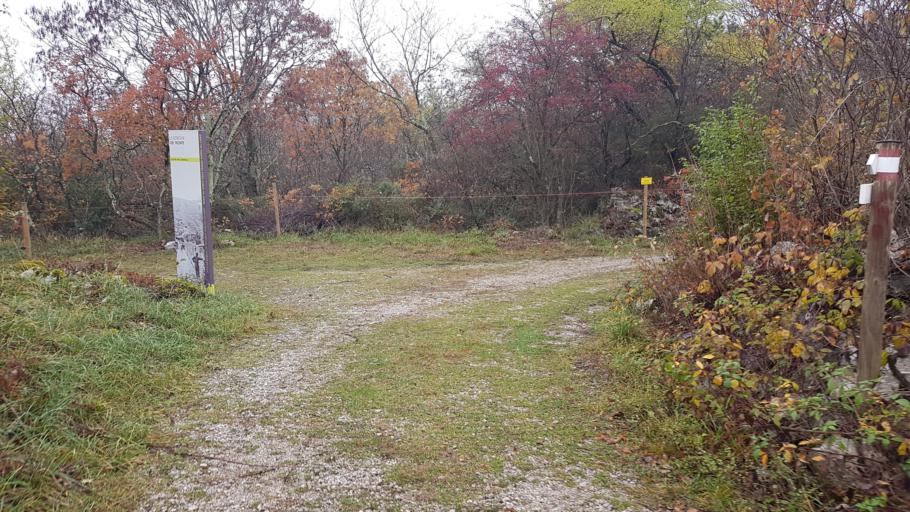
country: IT
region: Friuli Venezia Giulia
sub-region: Provincia di Gorizia
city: Doberdo del Lago
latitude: 45.8372
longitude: 13.5604
